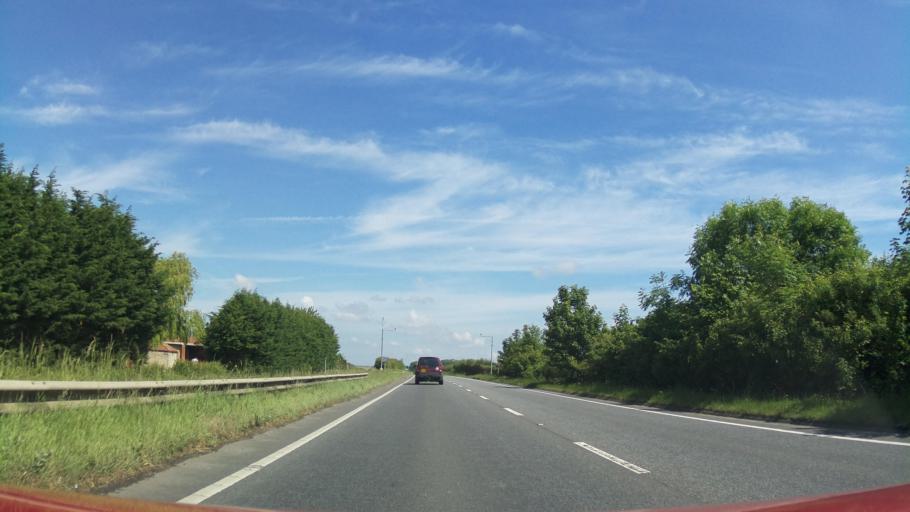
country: GB
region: England
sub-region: North Lincolnshire
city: Redbourne
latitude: 53.4752
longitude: -0.5523
